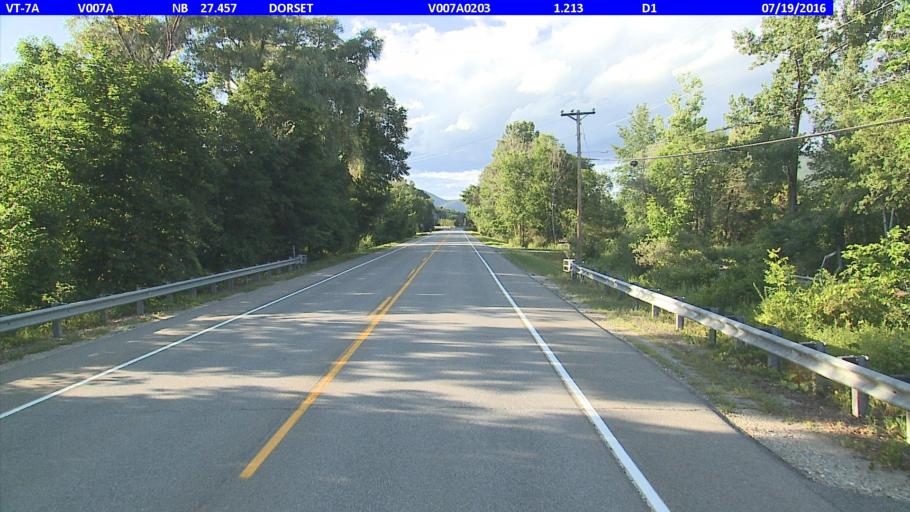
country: US
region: Vermont
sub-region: Bennington County
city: Manchester Center
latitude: 43.2270
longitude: -73.0113
